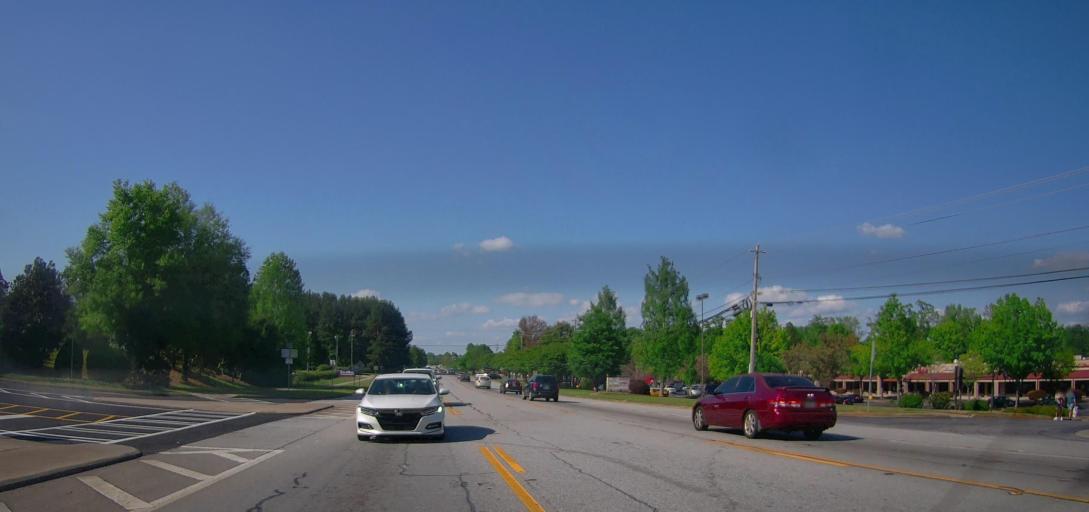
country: US
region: Georgia
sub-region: Morgan County
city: Madison
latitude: 33.5660
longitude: -83.4782
